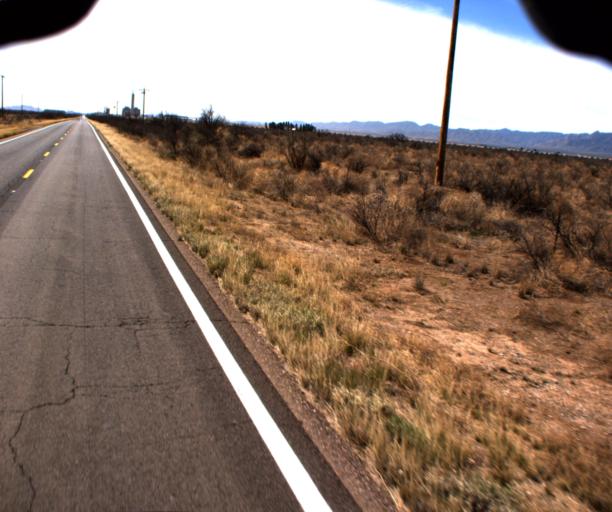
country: US
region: Arizona
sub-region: Cochise County
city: Willcox
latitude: 32.0891
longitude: -109.9057
